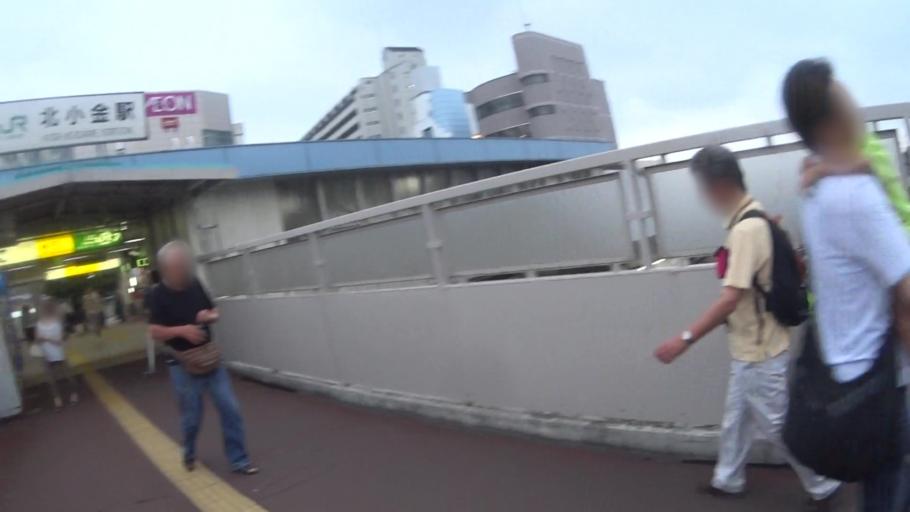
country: JP
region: Chiba
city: Nagareyama
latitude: 35.8336
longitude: 139.9312
